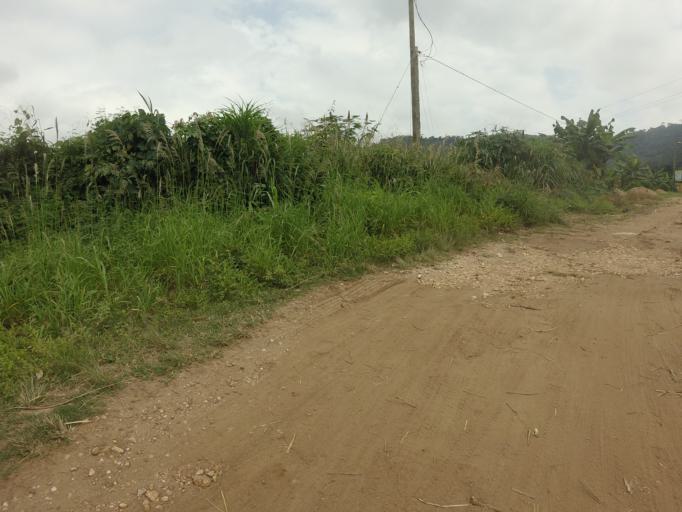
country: TG
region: Plateaux
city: Kpalime
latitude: 6.8640
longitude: 0.4417
